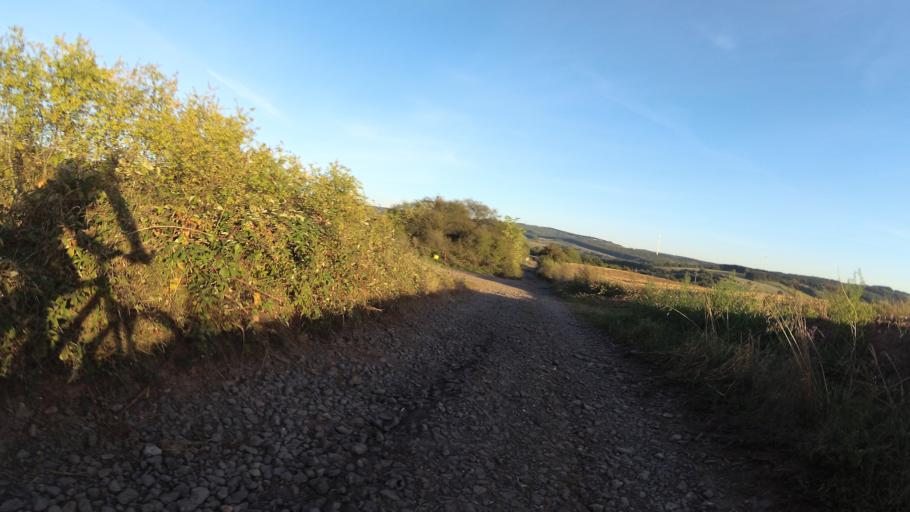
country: DE
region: Rheinland-Pfalz
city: Breitenbach
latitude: 49.4329
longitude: 7.2218
